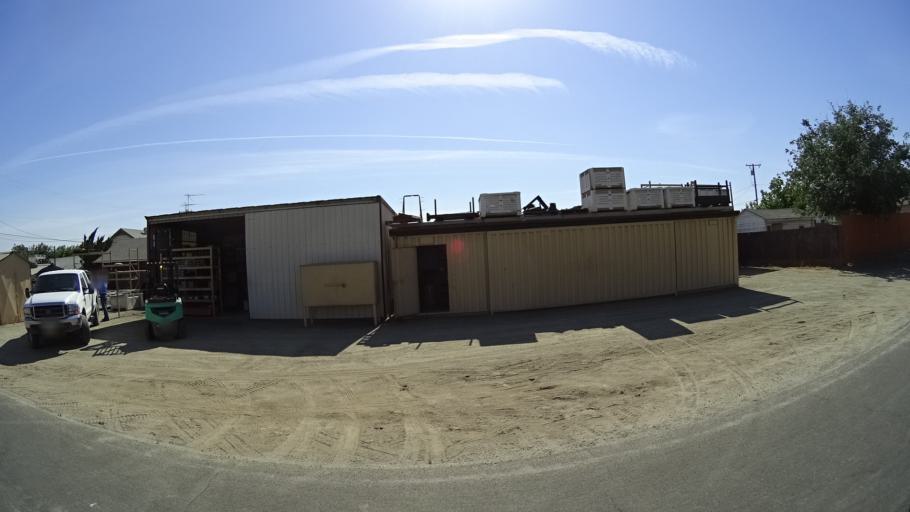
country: US
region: California
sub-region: Kings County
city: Hanford
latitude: 36.3254
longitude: -119.6361
